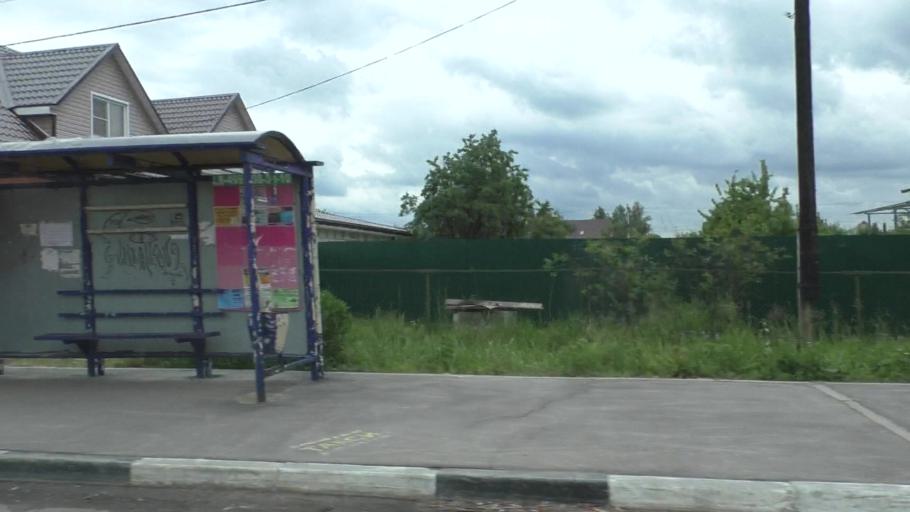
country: RU
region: Moskovskaya
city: Yegor'yevsk
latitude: 55.3998
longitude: 39.0088
